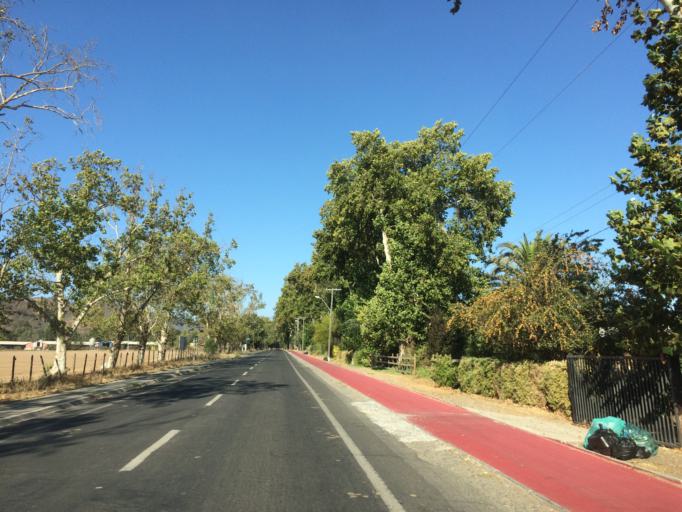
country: CL
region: Santiago Metropolitan
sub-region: Provincia de Melipilla
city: Melipilla
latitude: -33.4909
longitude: -71.1909
